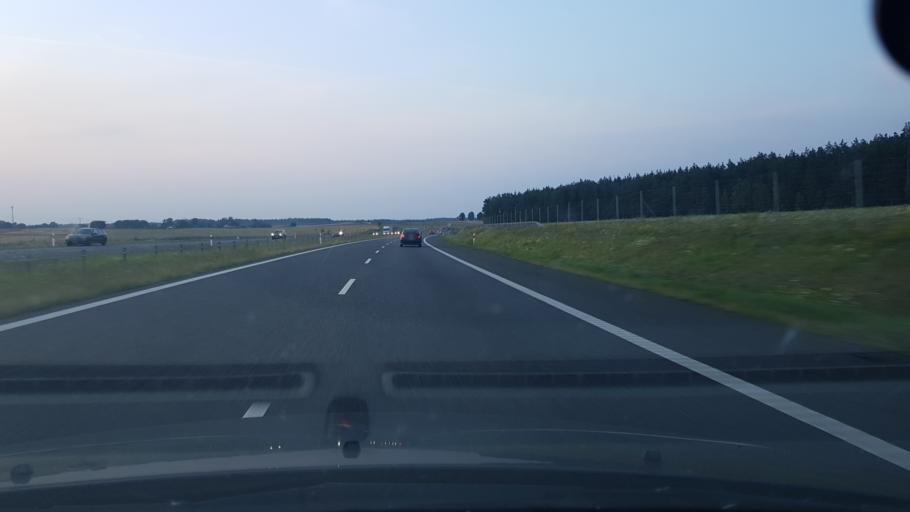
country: PL
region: Warmian-Masurian Voivodeship
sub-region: Powiat nidzicki
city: Nidzica
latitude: 53.4268
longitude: 20.3367
